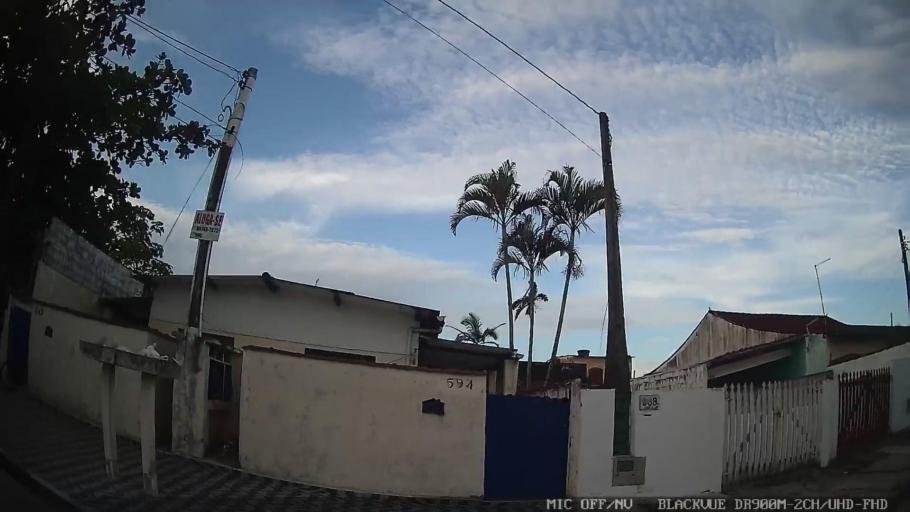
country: BR
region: Sao Paulo
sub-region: Itanhaem
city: Itanhaem
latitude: -24.1676
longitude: -46.7763
